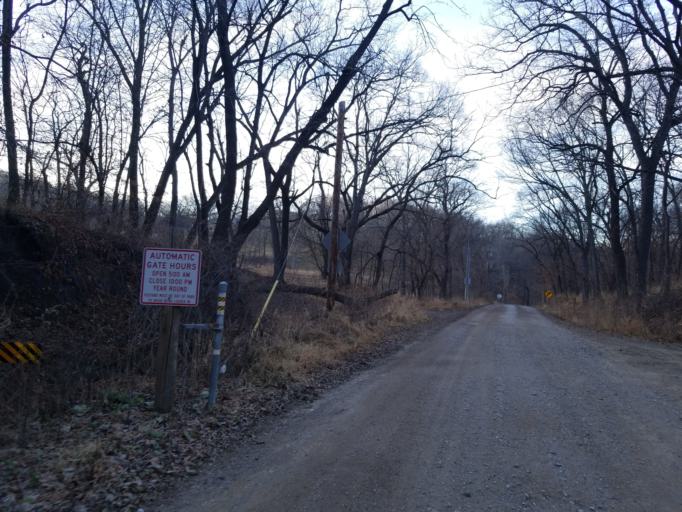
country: US
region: Nebraska
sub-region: Sarpy County
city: Bellevue
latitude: 41.1709
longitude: -95.9058
